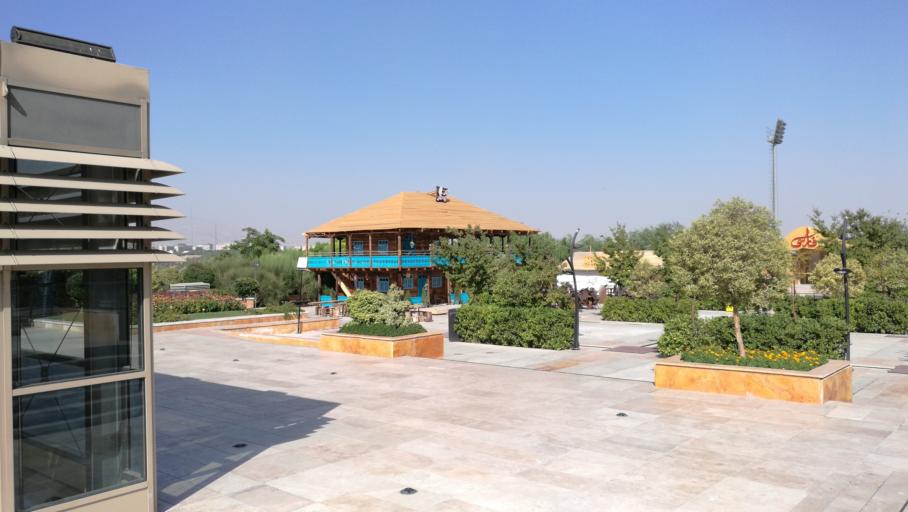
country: IR
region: Tehran
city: Tehran
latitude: 35.7455
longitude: 51.3759
